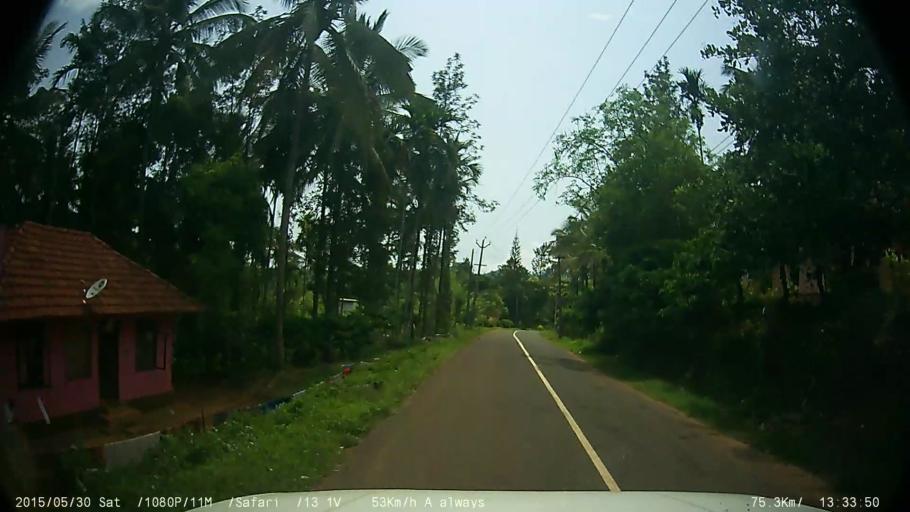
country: IN
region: Kerala
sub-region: Wayanad
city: Panamaram
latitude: 11.8217
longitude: 76.0690
